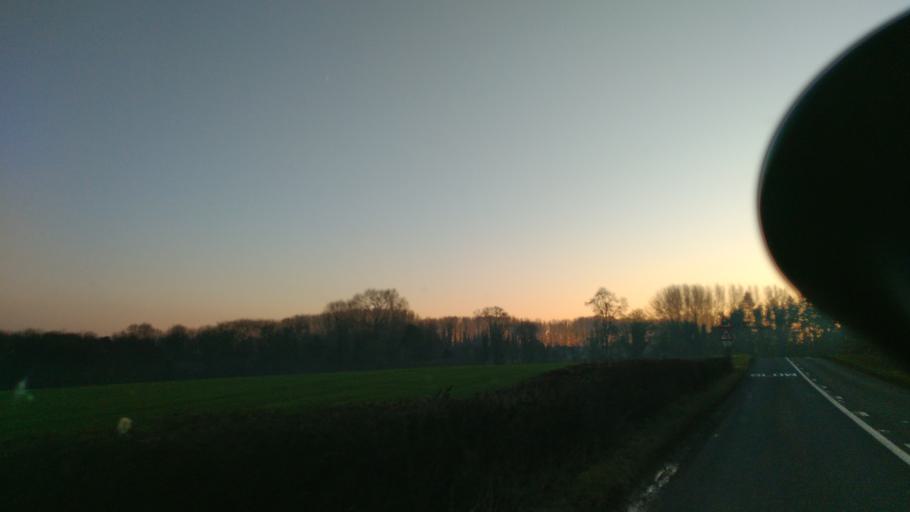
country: GB
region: England
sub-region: Wiltshire
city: Calne
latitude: 51.4114
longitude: -2.0245
